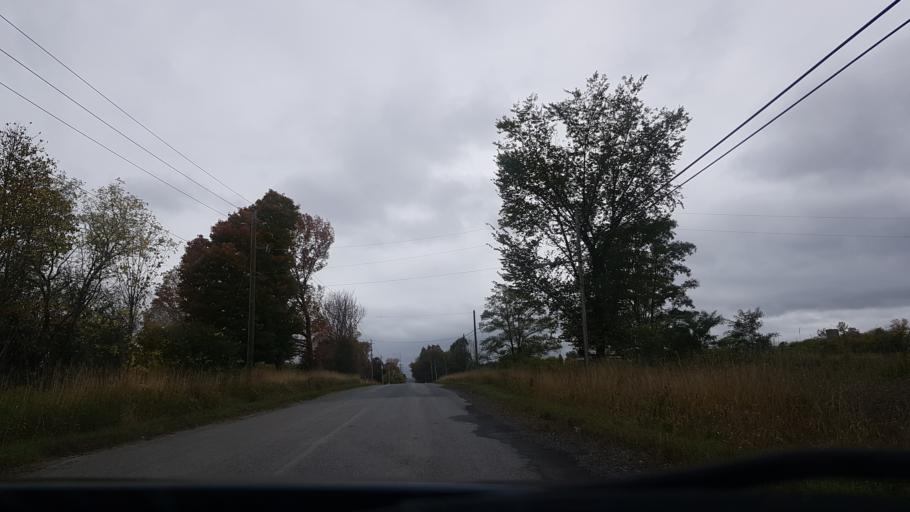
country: CA
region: Ontario
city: Peterborough
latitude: 44.2477
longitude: -78.4350
